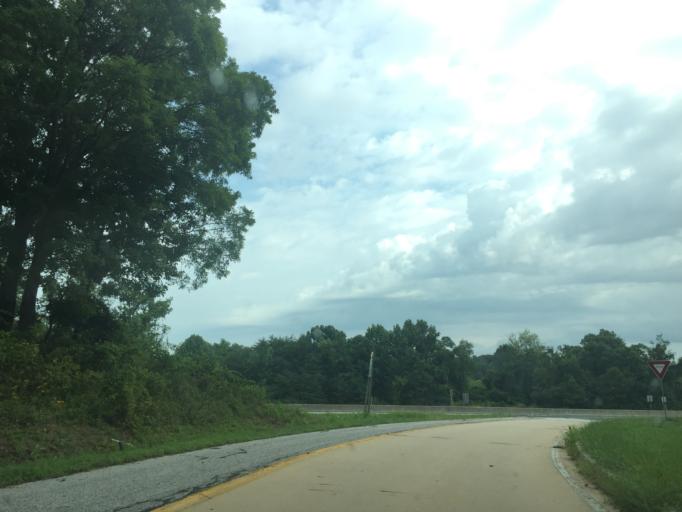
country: US
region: Maryland
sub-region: Baltimore County
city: Woodlawn
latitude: 39.3010
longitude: -76.7146
